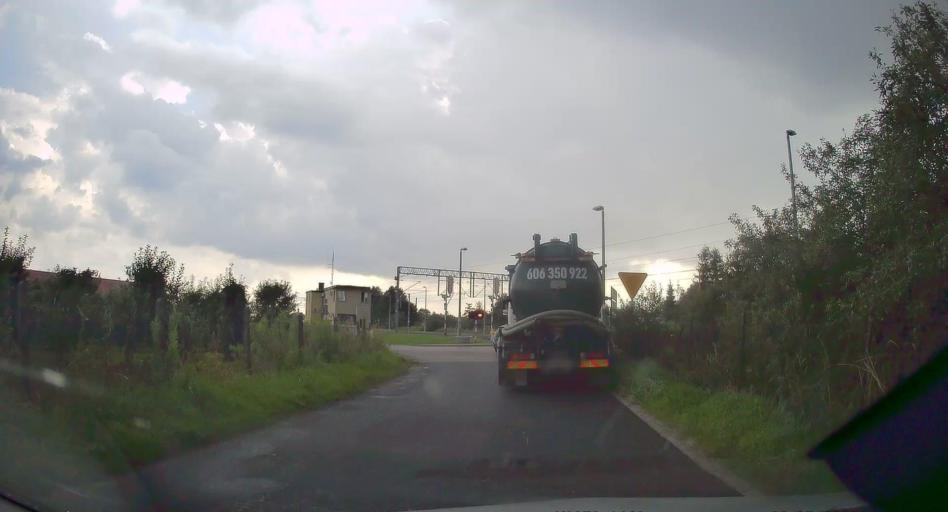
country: PL
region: Lodz Voivodeship
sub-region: Powiat brzezinski
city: Rogow
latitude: 51.8221
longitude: 19.8925
